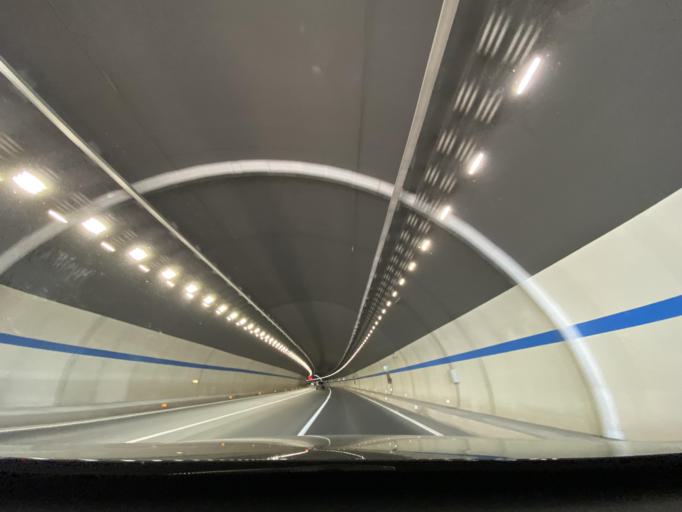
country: CN
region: Sichuan
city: Longquan
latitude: 30.4438
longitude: 104.2424
